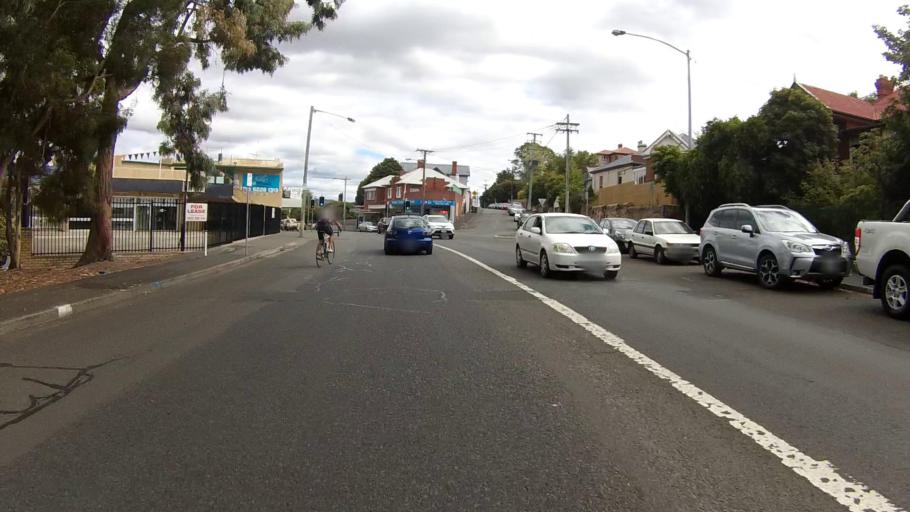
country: AU
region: Tasmania
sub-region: Hobart
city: New Town
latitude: -42.8621
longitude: 147.3105
